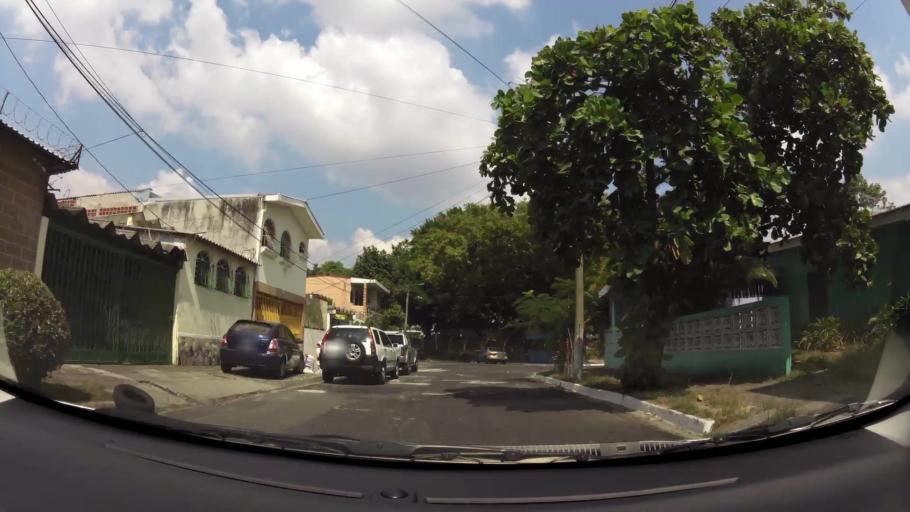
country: SV
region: San Salvador
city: Mejicanos
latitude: 13.7160
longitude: -89.2203
